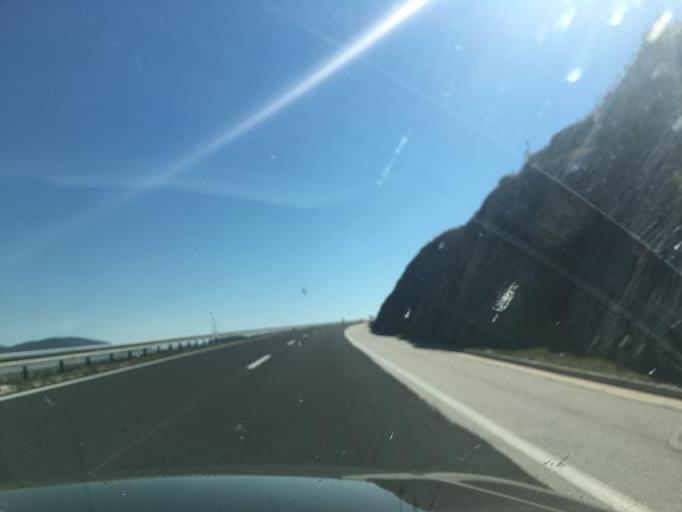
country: HR
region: Splitsko-Dalmatinska
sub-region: Grad Trogir
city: Trogir
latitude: 43.6317
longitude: 16.2260
